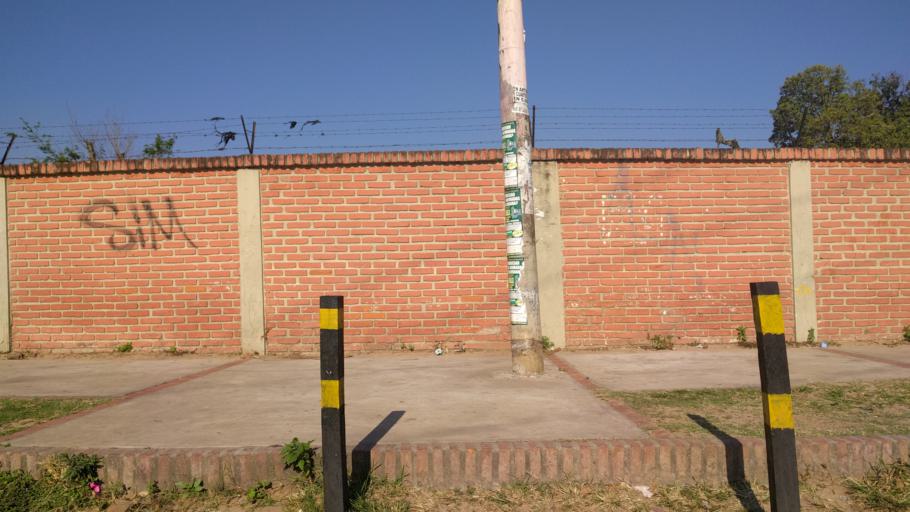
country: BO
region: Santa Cruz
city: Santa Cruz de la Sierra
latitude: -17.8127
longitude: -63.1905
